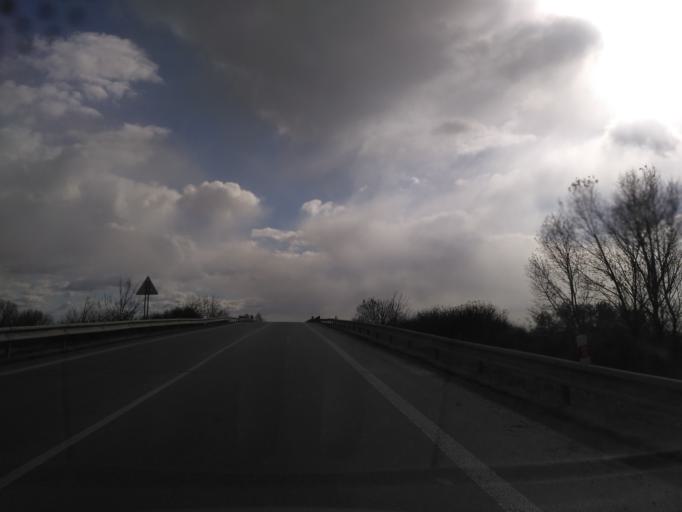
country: SK
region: Kosicky
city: Trebisov
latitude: 48.6270
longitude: 21.6963
